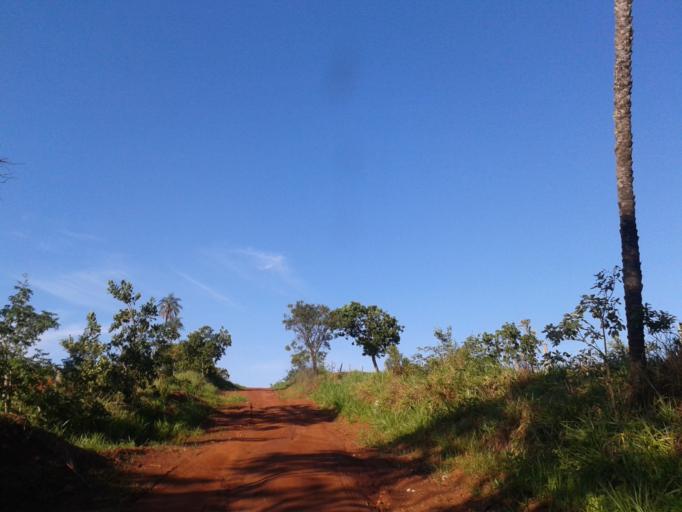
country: BR
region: Minas Gerais
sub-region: Santa Vitoria
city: Santa Vitoria
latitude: -18.9656
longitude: -49.8757
